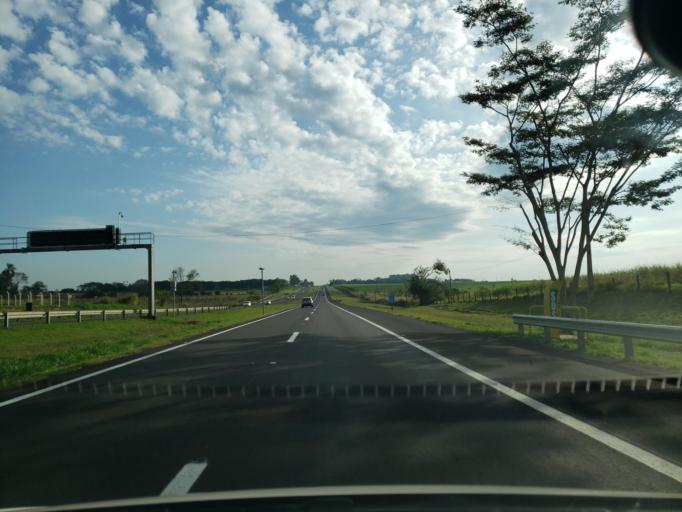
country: BR
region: Sao Paulo
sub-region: Guararapes
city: Guararapes
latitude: -21.2024
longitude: -50.5969
